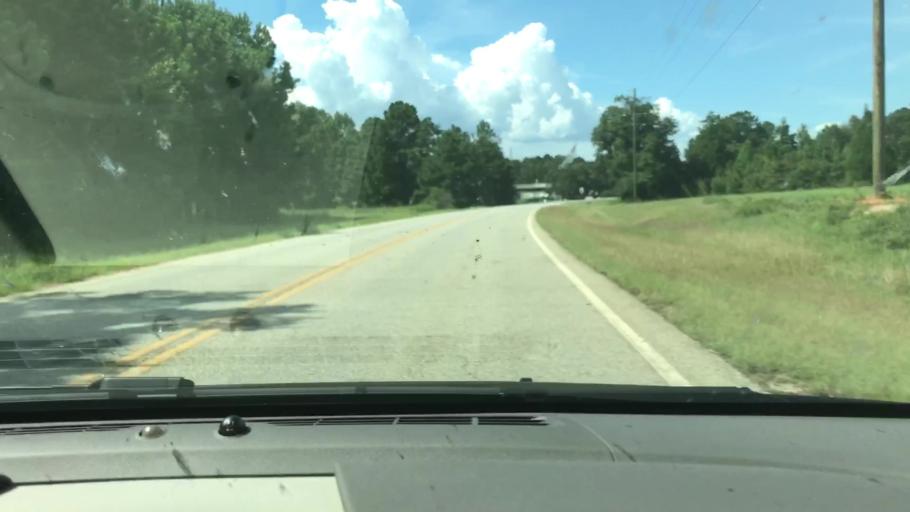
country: US
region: Georgia
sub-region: Quitman County
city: Georgetown
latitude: 31.7678
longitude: -85.0896
